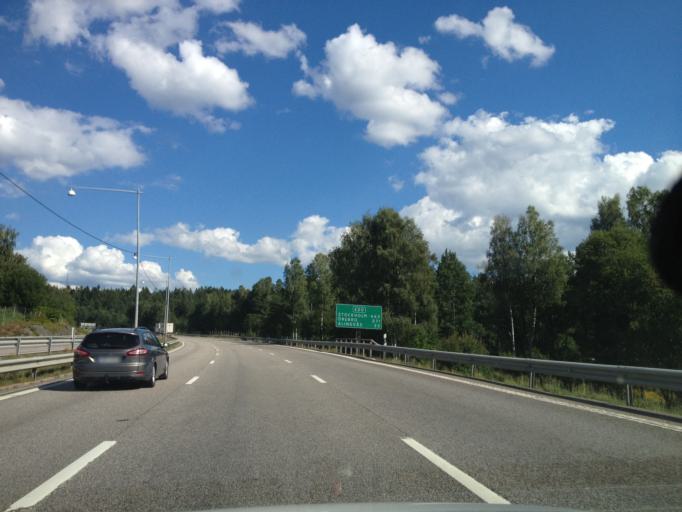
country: SE
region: Vaestra Goetaland
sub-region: Partille Kommun
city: Furulund
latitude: 57.7411
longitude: 12.1697
